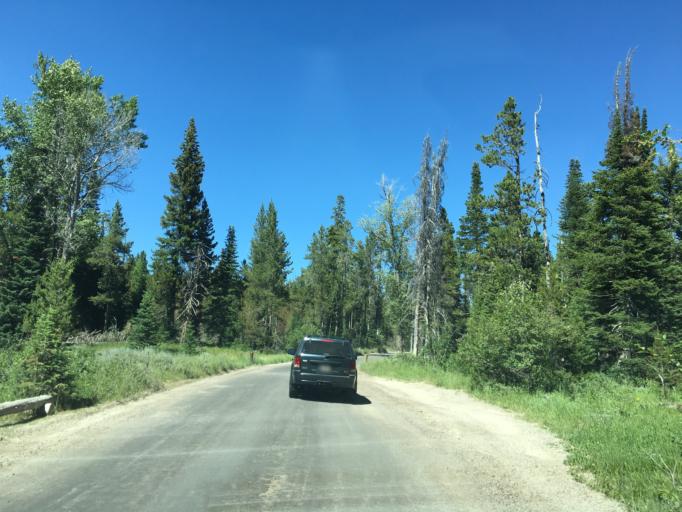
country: US
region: Wyoming
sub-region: Teton County
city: Moose Wilson Road
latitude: 43.6188
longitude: -110.7894
